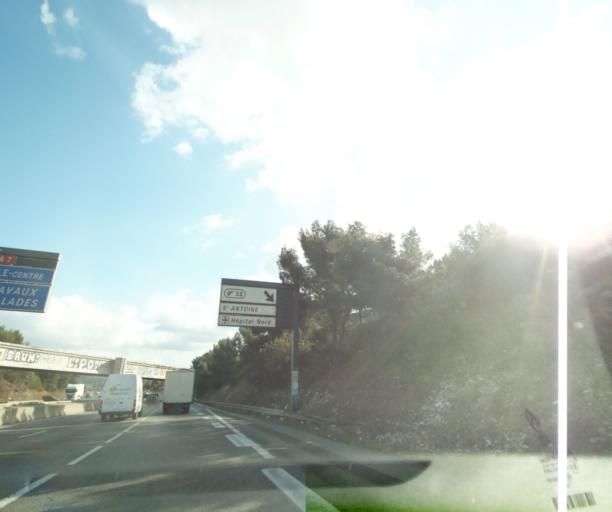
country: FR
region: Provence-Alpes-Cote d'Azur
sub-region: Departement des Bouches-du-Rhone
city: Marseille 15
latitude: 43.3800
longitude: 5.3533
